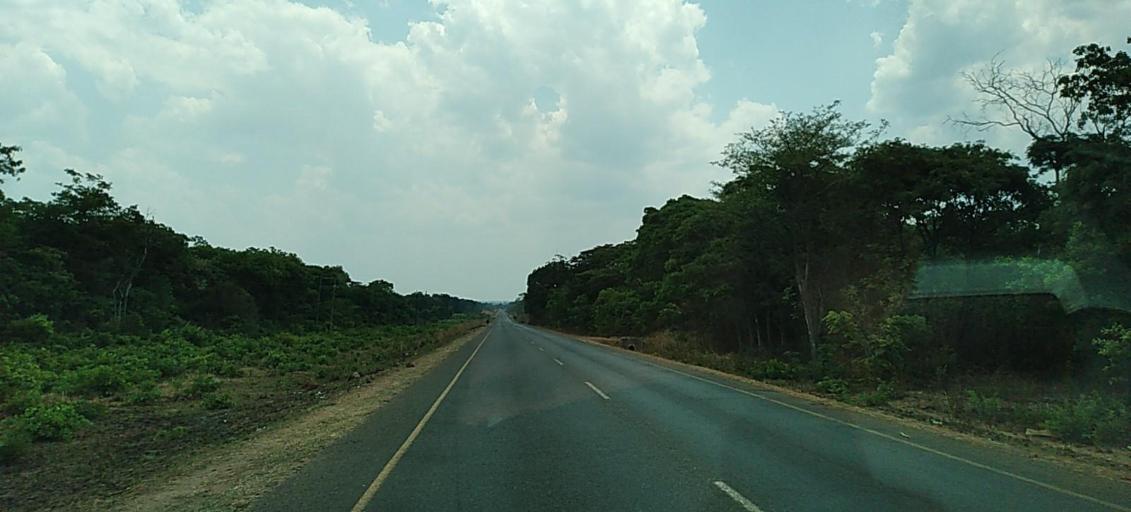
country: ZM
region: Copperbelt
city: Kalulushi
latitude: -12.8451
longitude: 28.0299
